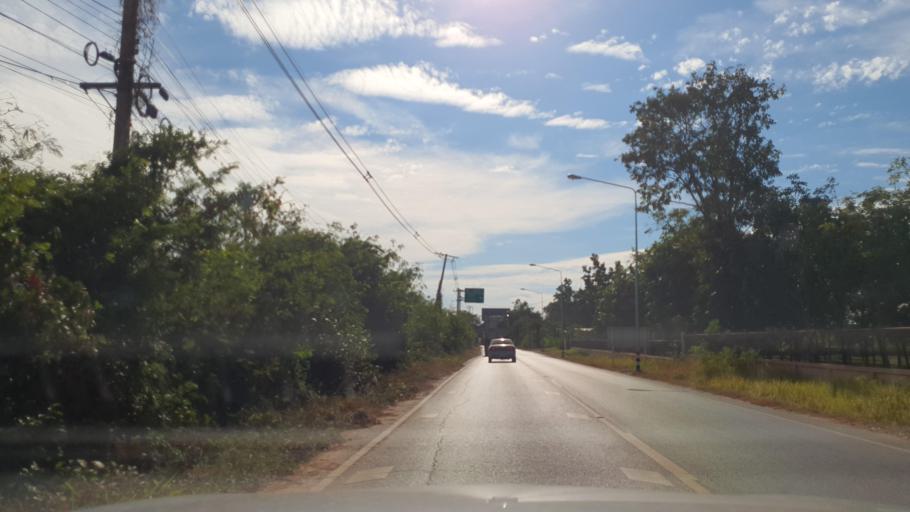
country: TH
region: Kalasin
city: Kuchinarai
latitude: 16.5355
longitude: 104.0746
